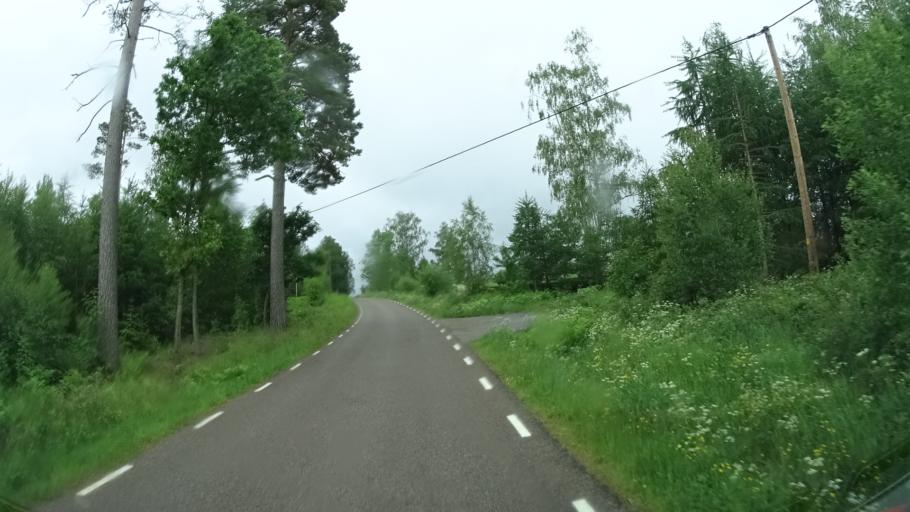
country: SE
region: Kalmar
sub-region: Vimmerby Kommun
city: Sodra Vi
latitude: 57.7074
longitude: 15.7586
